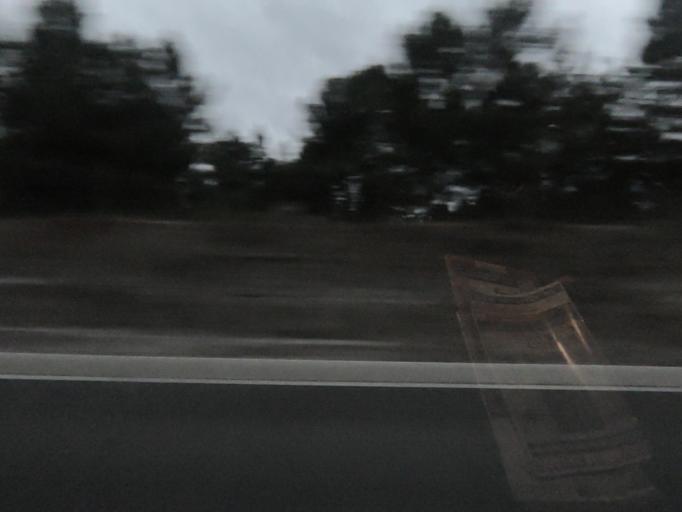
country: PT
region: Setubal
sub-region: Seixal
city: Arrentela
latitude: 38.6026
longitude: -9.1170
